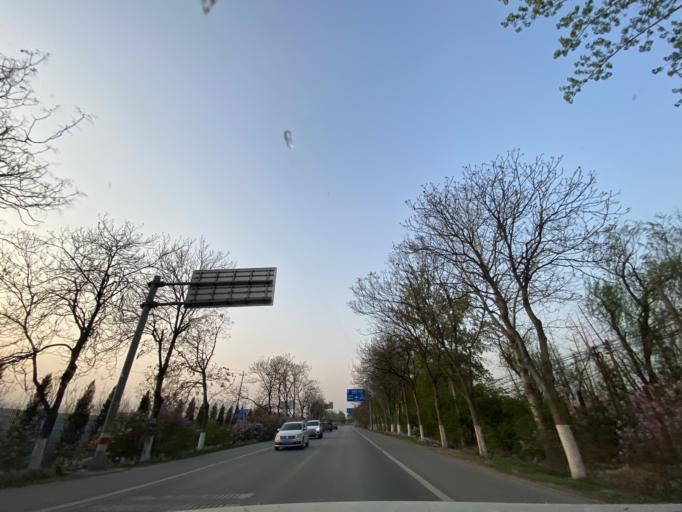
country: CN
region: Beijing
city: Weishanzhuang
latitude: 39.6130
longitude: 116.4095
